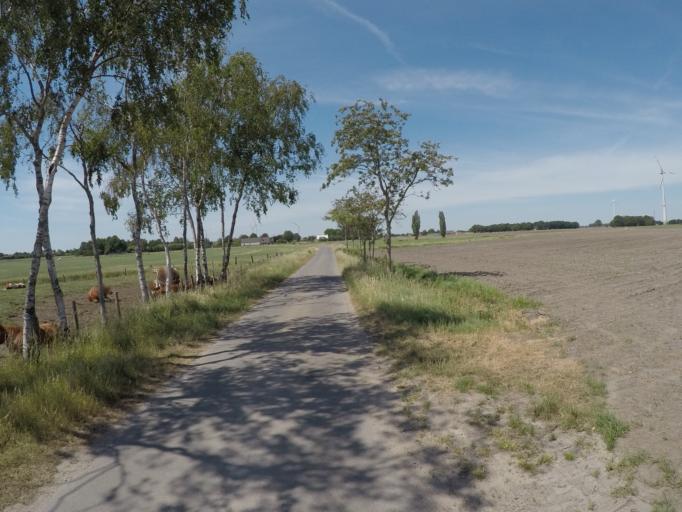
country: BE
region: Flanders
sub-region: Provincie Antwerpen
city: Hoogstraten
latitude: 51.3881
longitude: 4.6967
